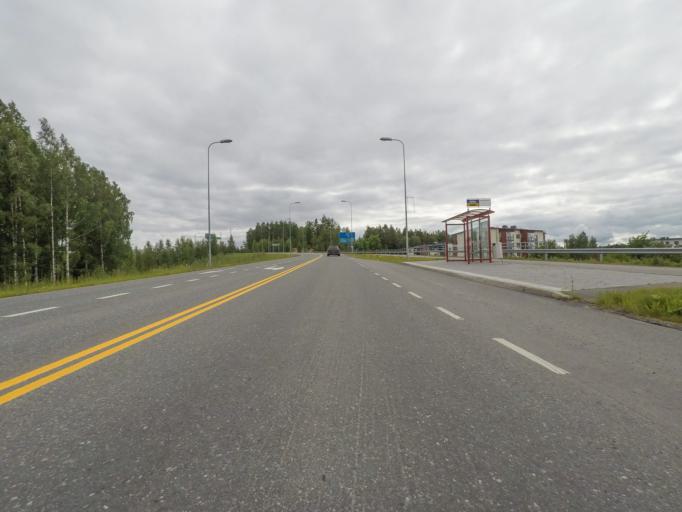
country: FI
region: Northern Savo
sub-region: Kuopio
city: Kuopio
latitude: 62.9743
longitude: 27.7026
